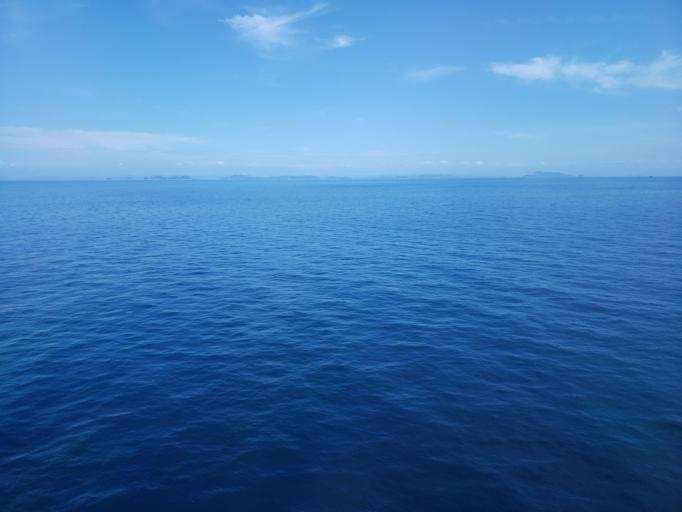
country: JP
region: Hyogo
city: Fukura
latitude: 34.4951
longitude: 134.5733
